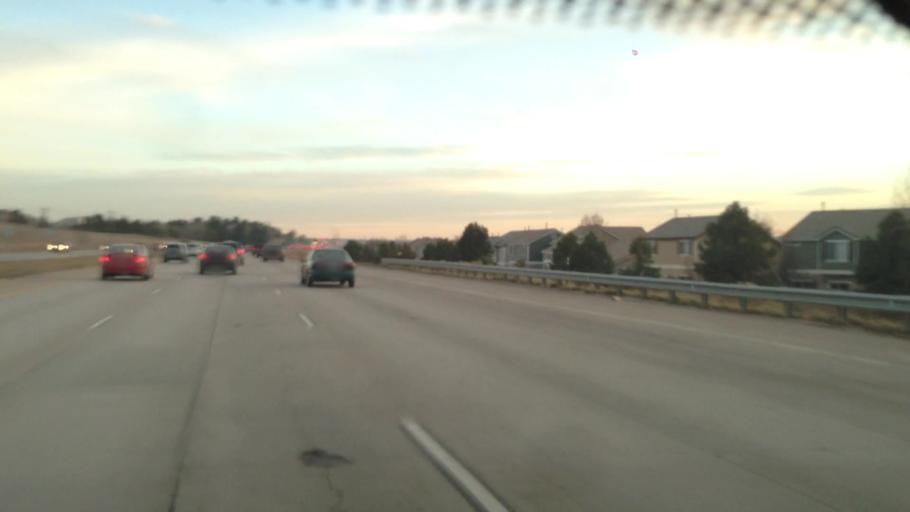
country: US
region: Colorado
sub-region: Arapahoe County
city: Dove Valley
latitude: 39.5841
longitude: -104.7958
